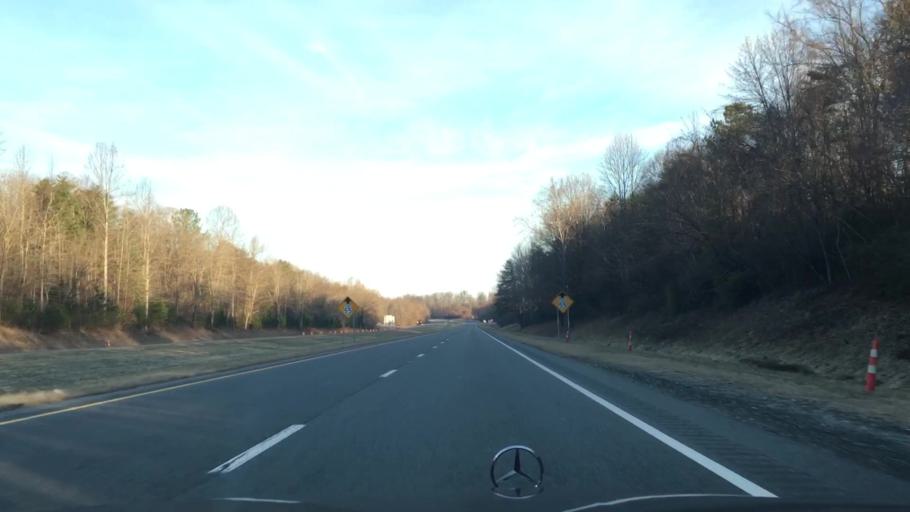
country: US
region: North Carolina
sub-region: Guilford County
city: Pleasant Garden
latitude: 36.0141
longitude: -79.7607
